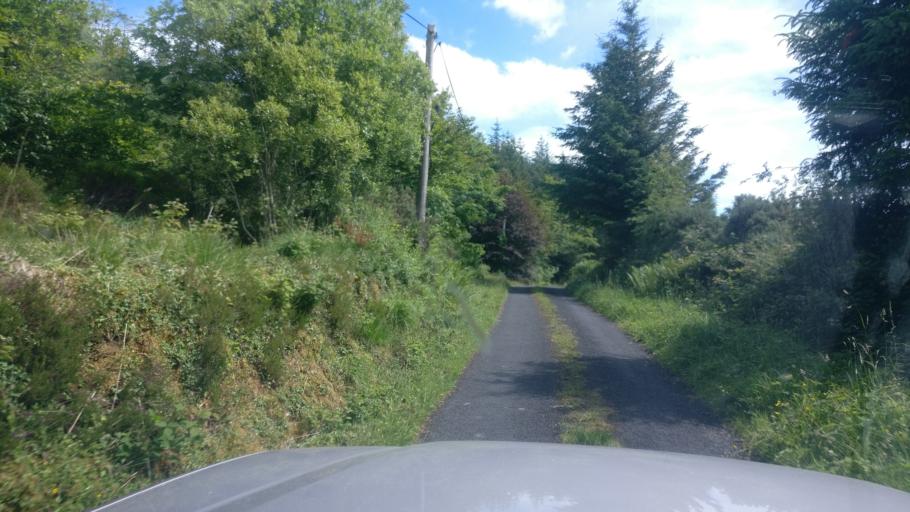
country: IE
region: Connaught
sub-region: County Galway
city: Gort
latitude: 53.0759
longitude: -8.7091
